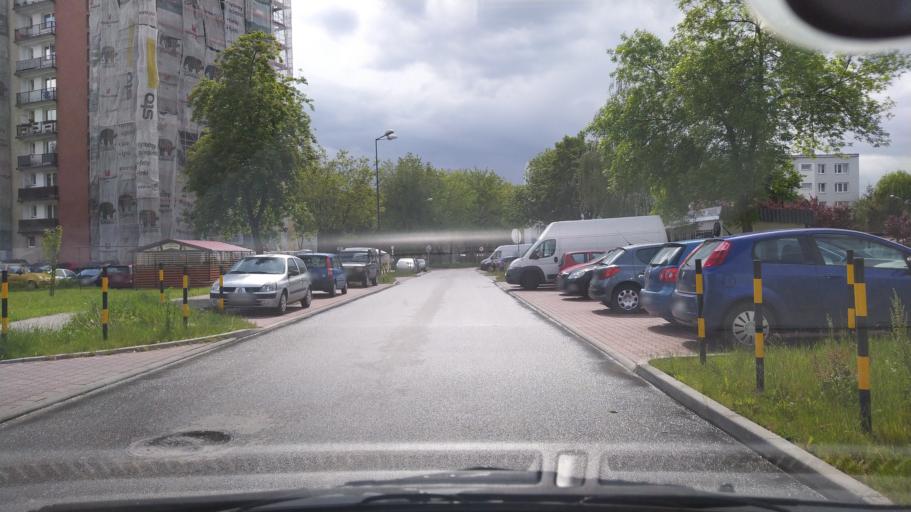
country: PL
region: Silesian Voivodeship
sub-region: Powiat gliwicki
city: Przyszowice
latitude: 50.2856
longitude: 18.7322
